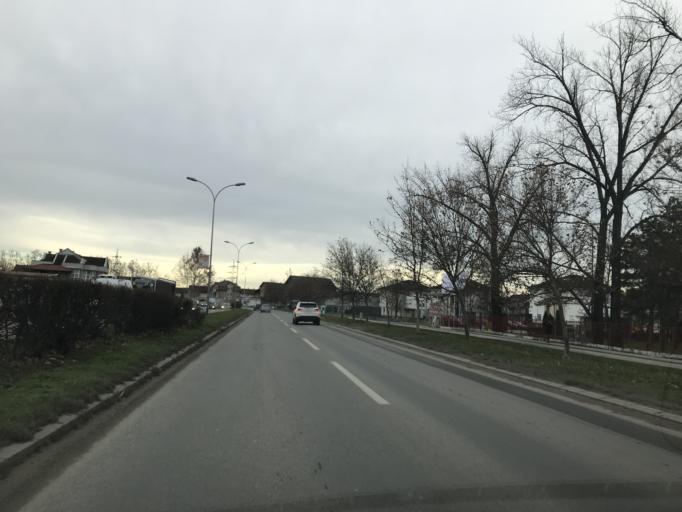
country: RS
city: Veternik
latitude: 45.2447
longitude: 19.7759
